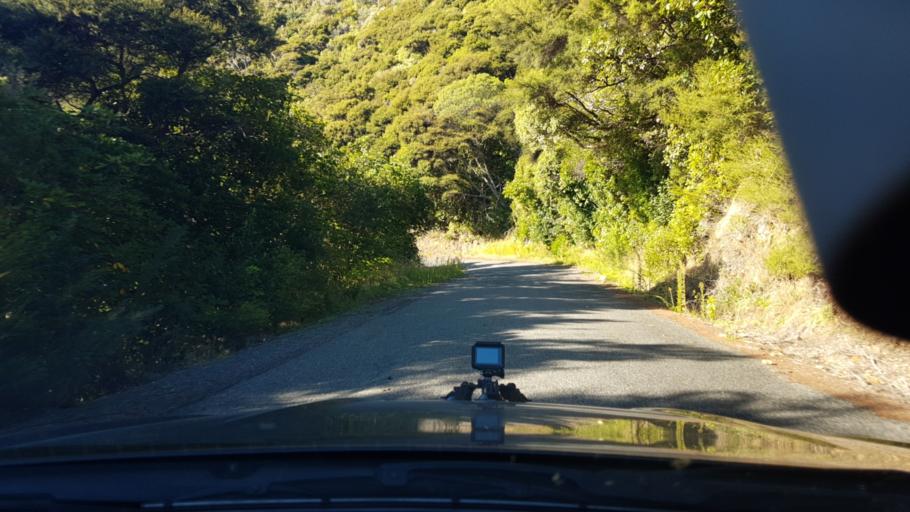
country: NZ
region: Marlborough
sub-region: Marlborough District
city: Picton
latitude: -40.9251
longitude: 173.8387
